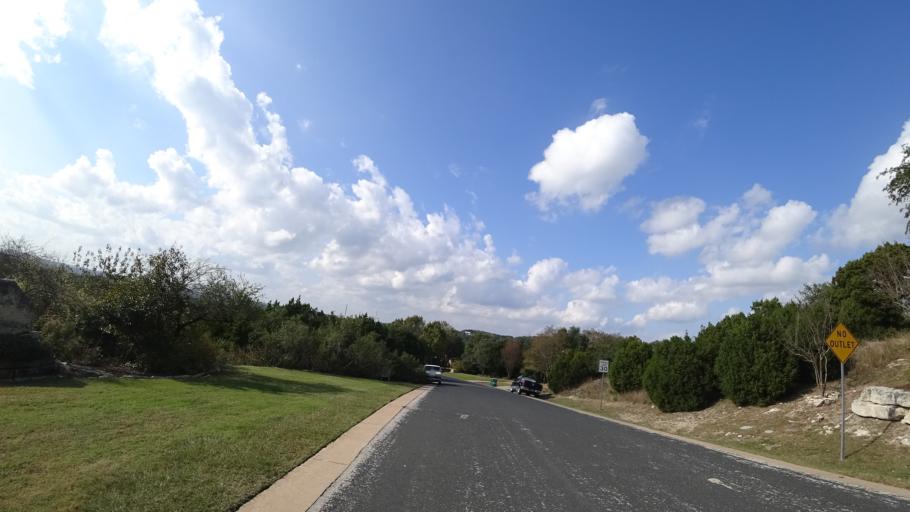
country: US
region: Texas
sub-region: Travis County
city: Lost Creek
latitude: 30.3034
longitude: -97.8437
